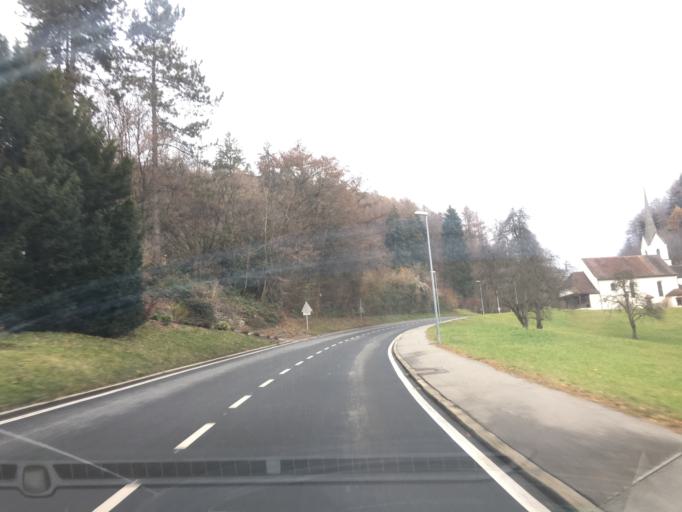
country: AT
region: Vorarlberg
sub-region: Politischer Bezirk Feldkirch
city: Gotzis
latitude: 47.3239
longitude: 9.6433
